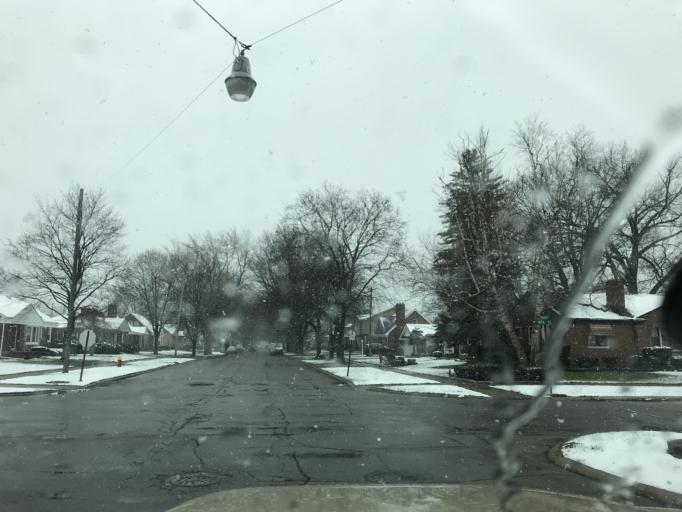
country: US
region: Michigan
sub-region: Wayne County
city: Allen Park
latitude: 42.2425
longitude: -83.2192
